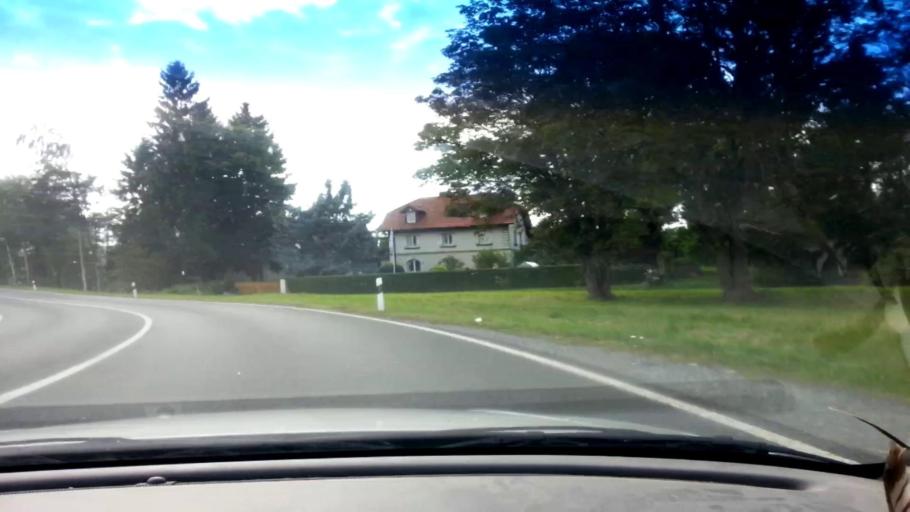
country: DE
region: Bavaria
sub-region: Upper Franconia
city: Marktredwitz
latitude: 50.0163
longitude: 12.1016
